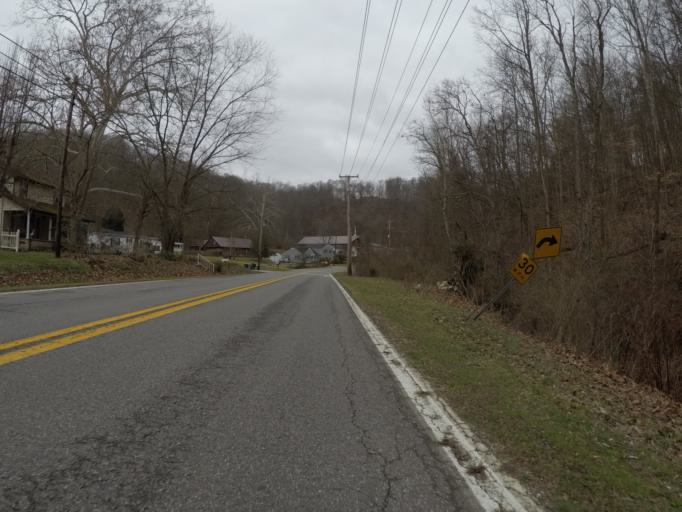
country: US
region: West Virginia
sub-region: Cabell County
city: Barboursville
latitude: 38.4547
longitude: -82.2979
